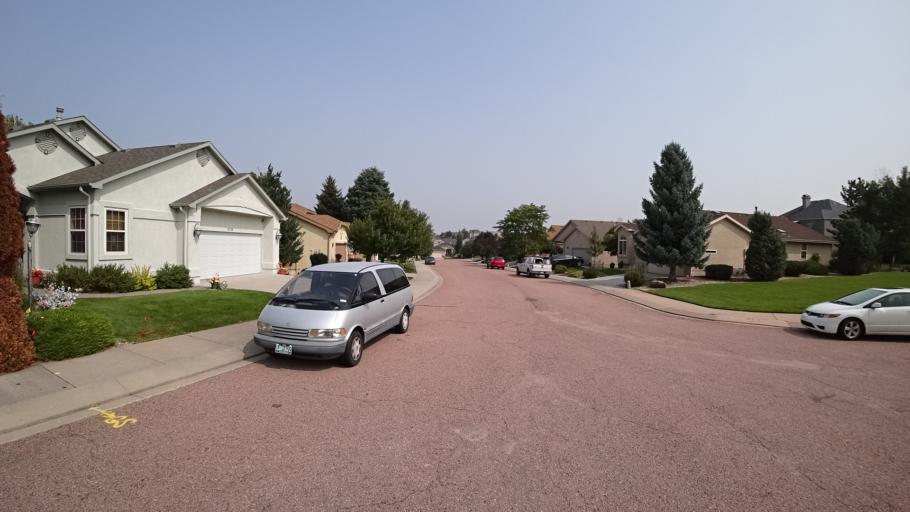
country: US
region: Colorado
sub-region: El Paso County
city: Cimarron Hills
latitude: 38.9204
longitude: -104.7444
